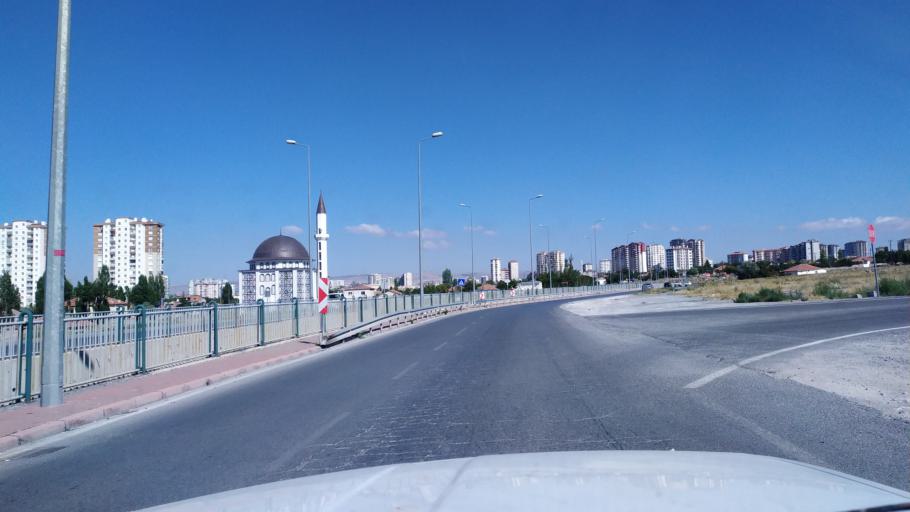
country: TR
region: Kayseri
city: Talas
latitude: 38.7299
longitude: 35.5495
